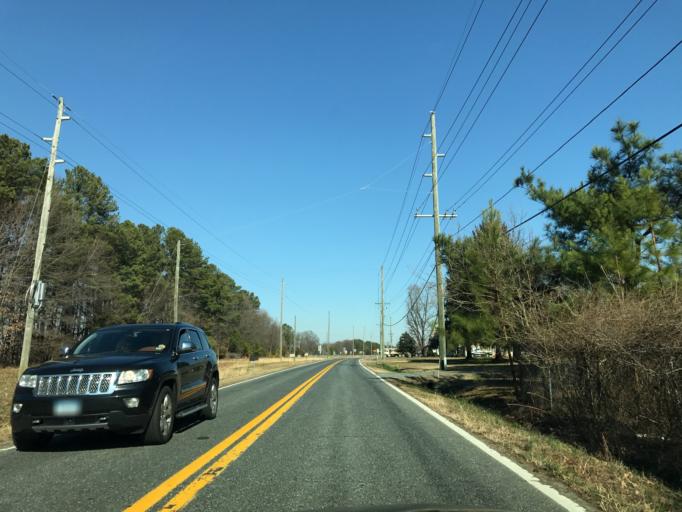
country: US
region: Maryland
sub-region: Queen Anne's County
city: Grasonville
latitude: 38.9825
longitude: -76.1638
